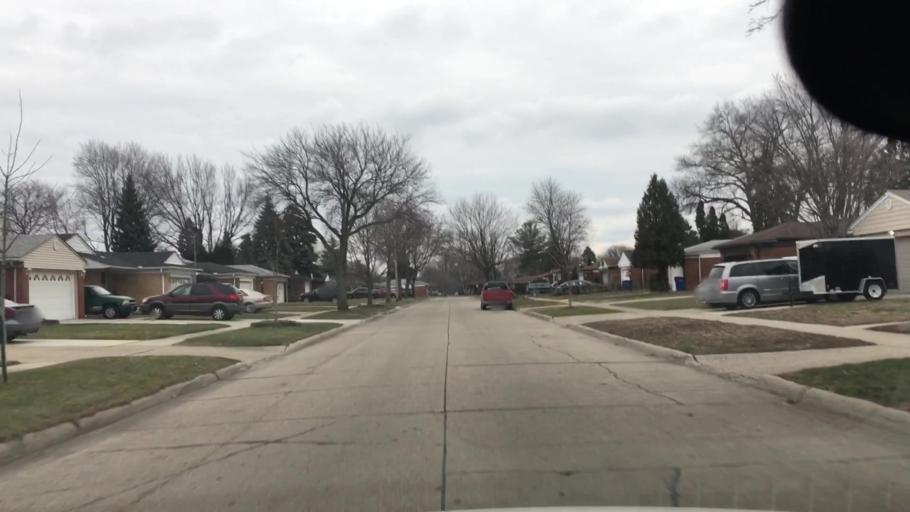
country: US
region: Michigan
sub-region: Oakland County
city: Madison Heights
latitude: 42.4973
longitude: -83.0712
